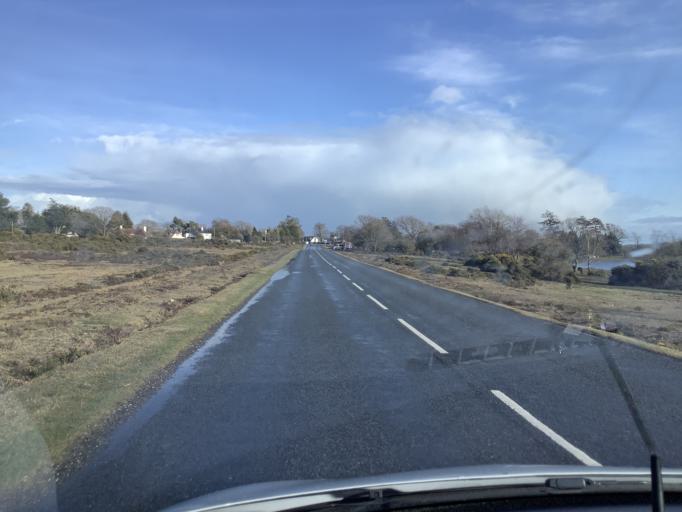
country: GB
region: England
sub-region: Hampshire
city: Marchwood
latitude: 50.8143
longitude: -1.4808
